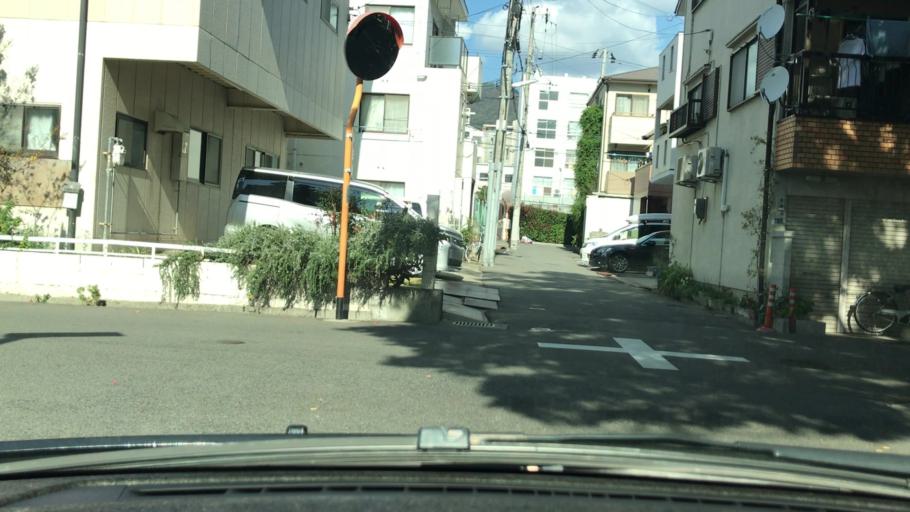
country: JP
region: Hyogo
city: Kobe
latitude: 34.7035
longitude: 135.2183
